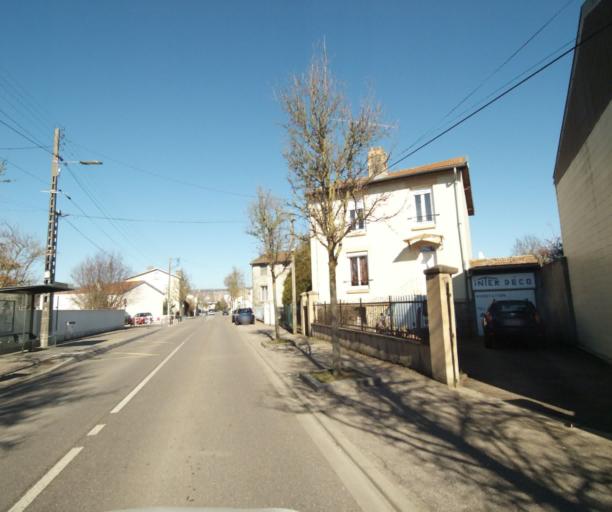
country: FR
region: Lorraine
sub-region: Departement de Meurthe-et-Moselle
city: Tomblaine
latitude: 48.6909
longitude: 6.2108
